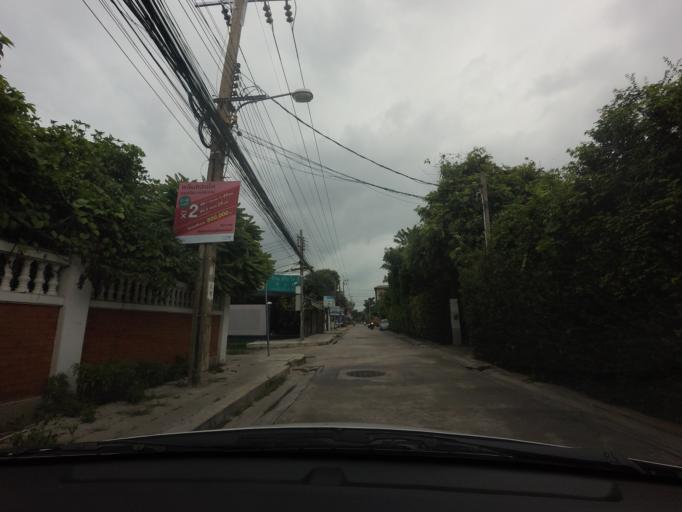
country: TH
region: Bangkok
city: Lak Si
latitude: 13.8954
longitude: 100.5631
